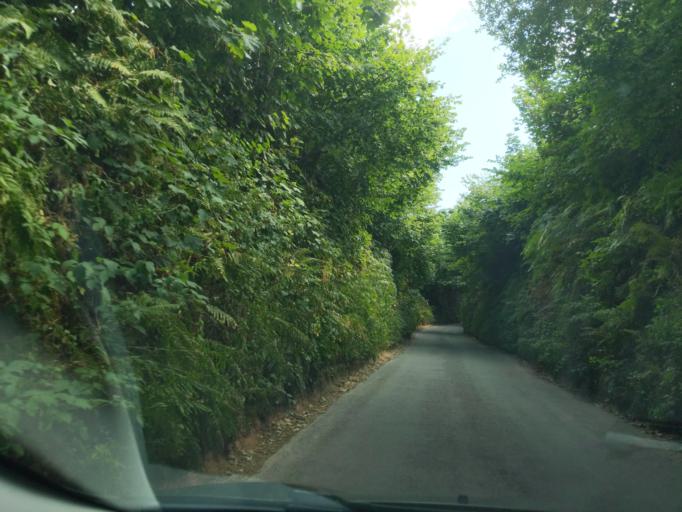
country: GB
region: England
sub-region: Devon
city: Modbury
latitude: 50.3574
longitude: -3.8894
